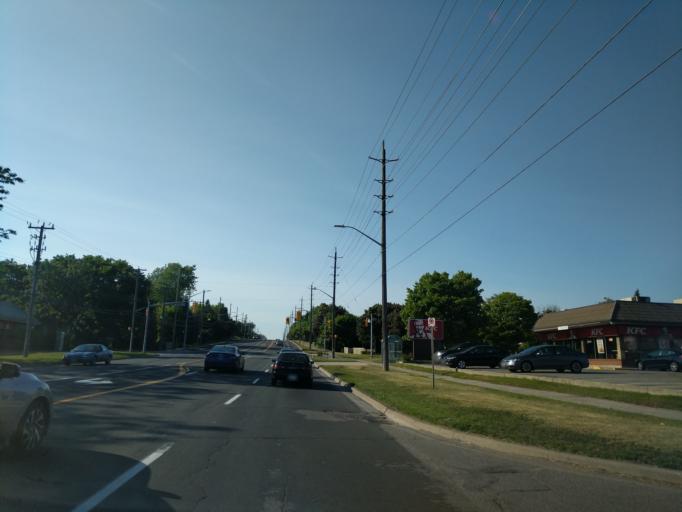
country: CA
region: Ontario
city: Oshawa
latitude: 43.8878
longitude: -78.9133
